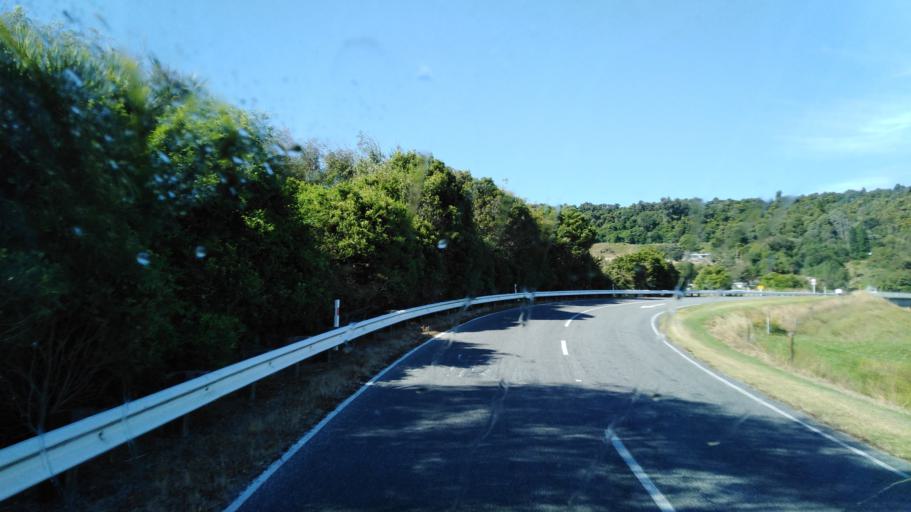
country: NZ
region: West Coast
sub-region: Buller District
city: Westport
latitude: -41.2594
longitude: 172.1324
